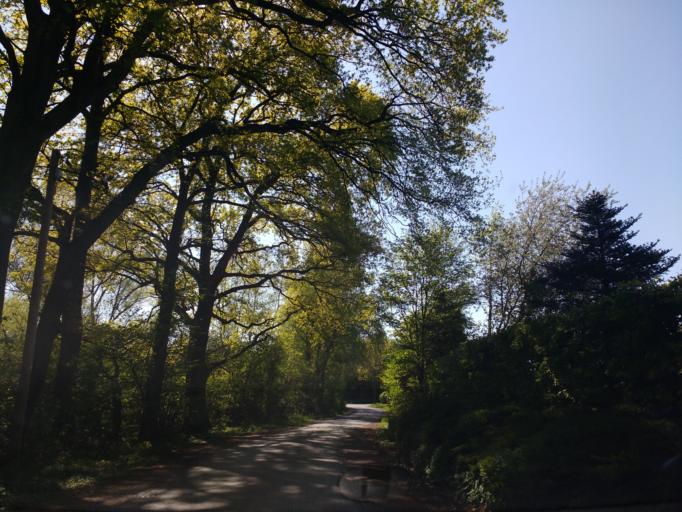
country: DE
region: North Rhine-Westphalia
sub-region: Regierungsbezirk Detmold
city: Delbruck
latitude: 51.7651
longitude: 8.5832
